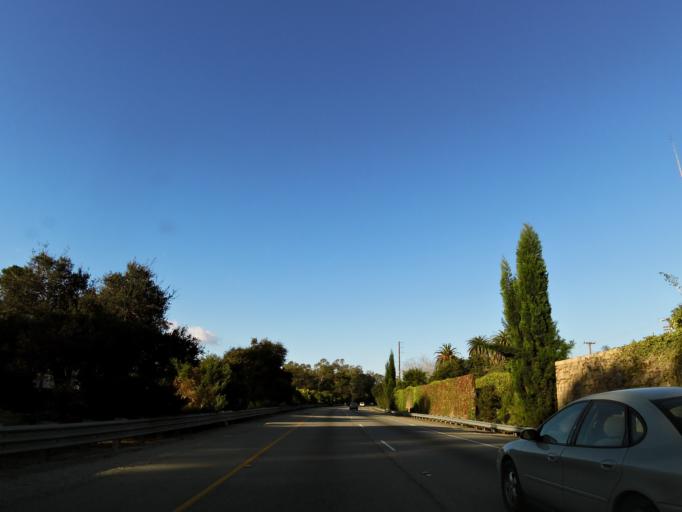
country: US
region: California
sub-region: Santa Barbara County
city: Toro Canyon
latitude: 34.4159
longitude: -119.5733
